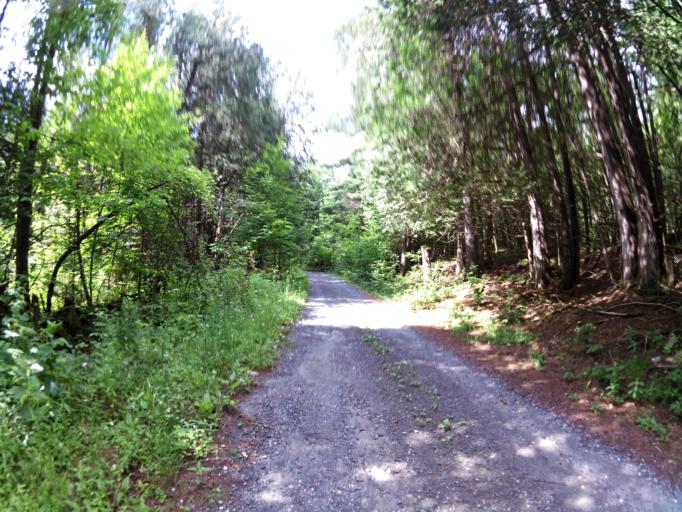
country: CA
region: Ontario
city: Perth
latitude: 45.0678
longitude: -76.4758
